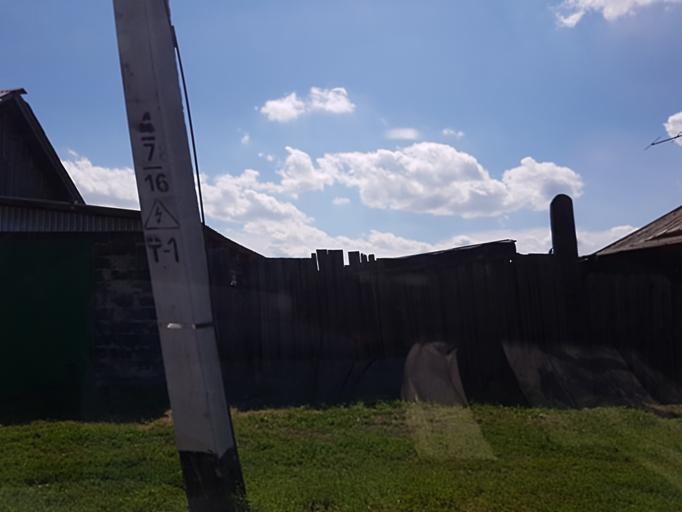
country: RU
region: Irkutsk
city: Kitoy
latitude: 52.6024
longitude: 103.8254
